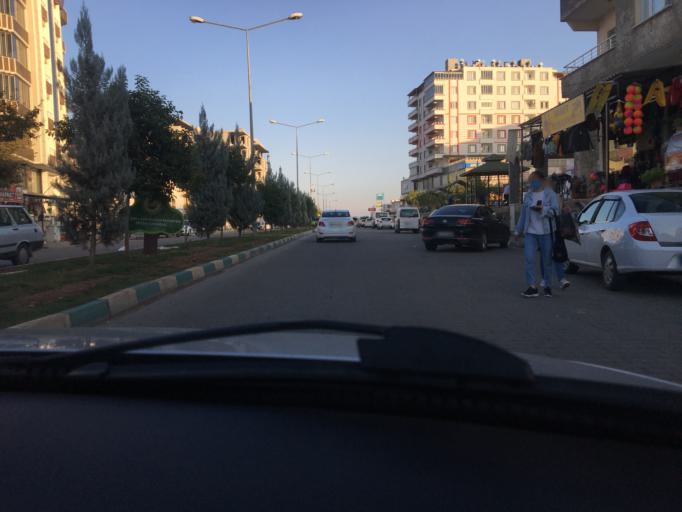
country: TR
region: Sanliurfa
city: Halfeti
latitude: 37.2312
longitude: 37.9448
